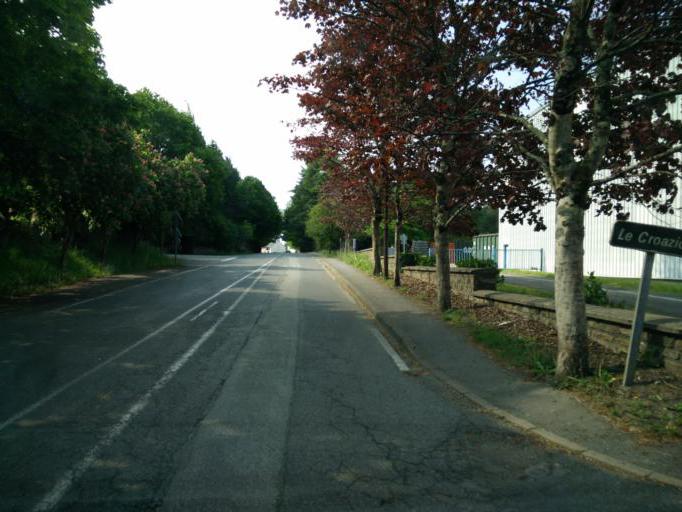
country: FR
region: Brittany
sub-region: Departement du Finistere
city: Moelan-sur-Mer
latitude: 47.8075
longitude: -3.6278
